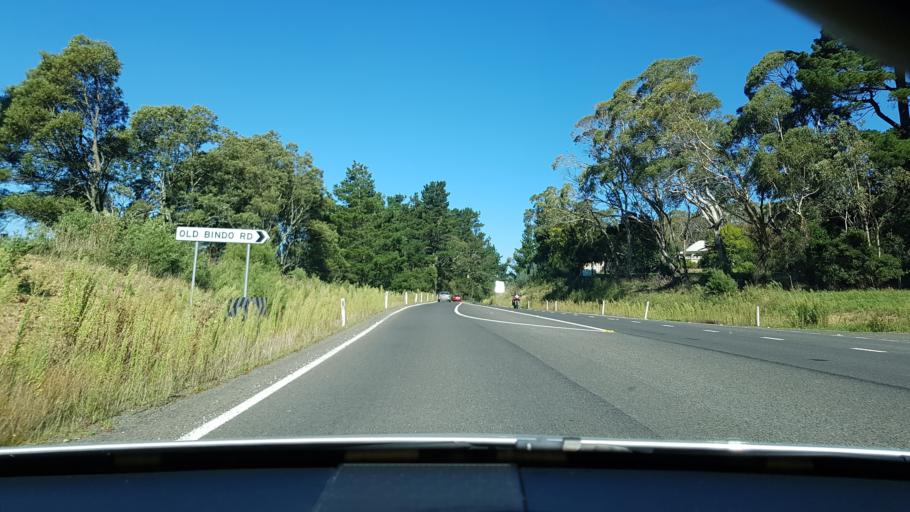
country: AU
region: New South Wales
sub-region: Lithgow
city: Bowenfels
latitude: -33.6473
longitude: 150.0483
